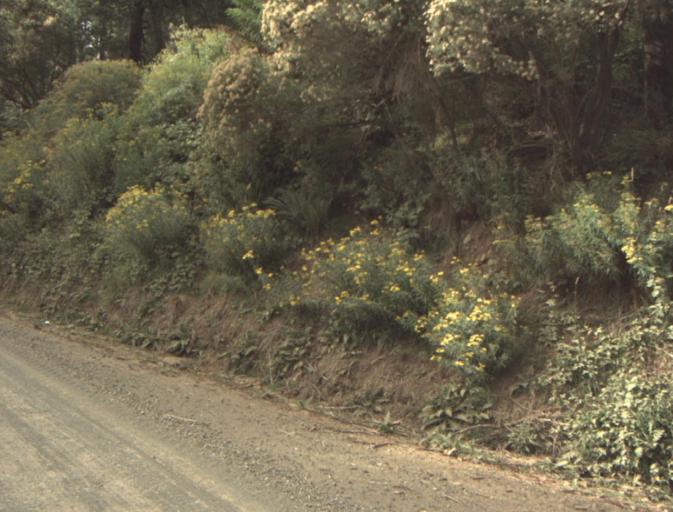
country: AU
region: Tasmania
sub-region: Dorset
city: Scottsdale
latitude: -41.3309
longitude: 147.4280
